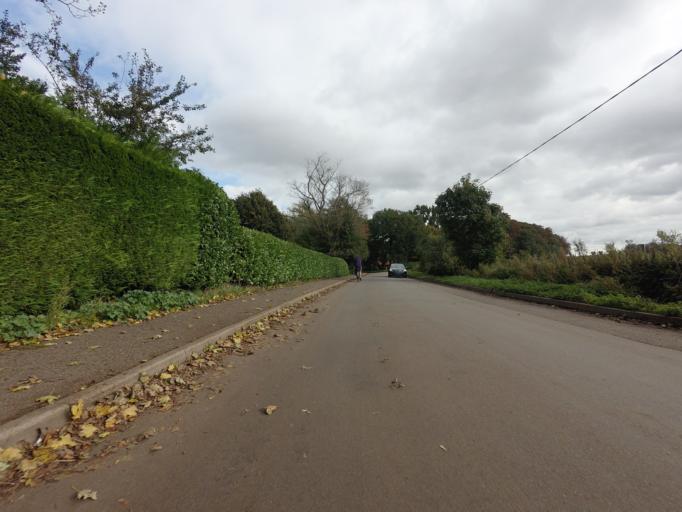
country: GB
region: England
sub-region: Norfolk
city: Snettisham
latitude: 52.8648
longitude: 0.5084
